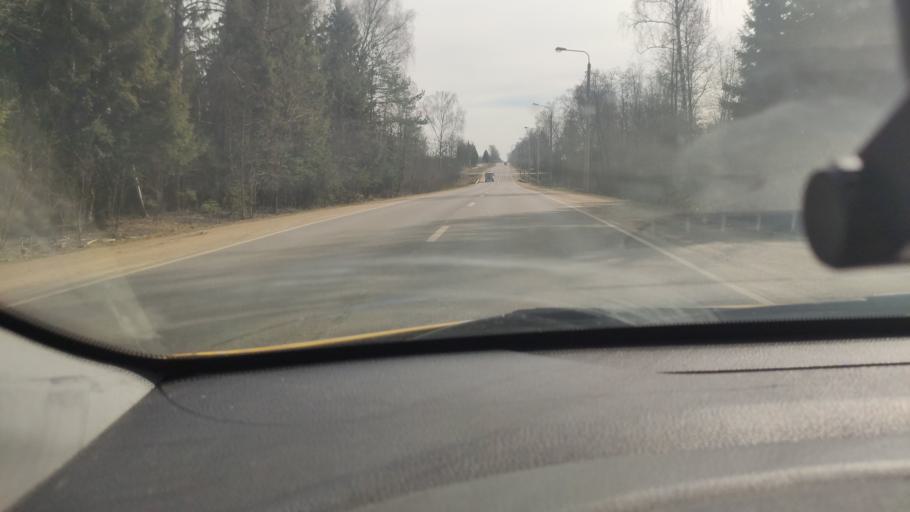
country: RU
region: Moskovskaya
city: Ruza
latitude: 55.7189
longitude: 36.1660
